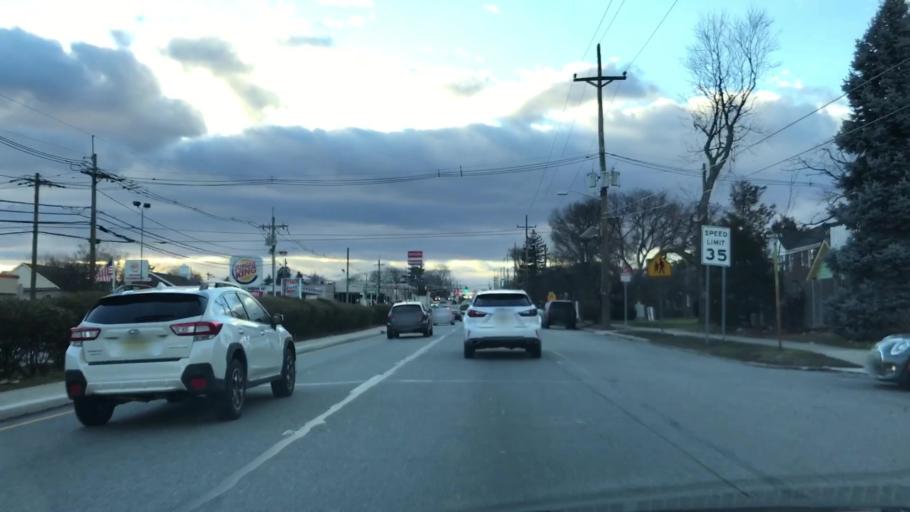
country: US
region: New Jersey
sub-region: Passaic County
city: Clifton
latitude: 40.8789
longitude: -74.1539
